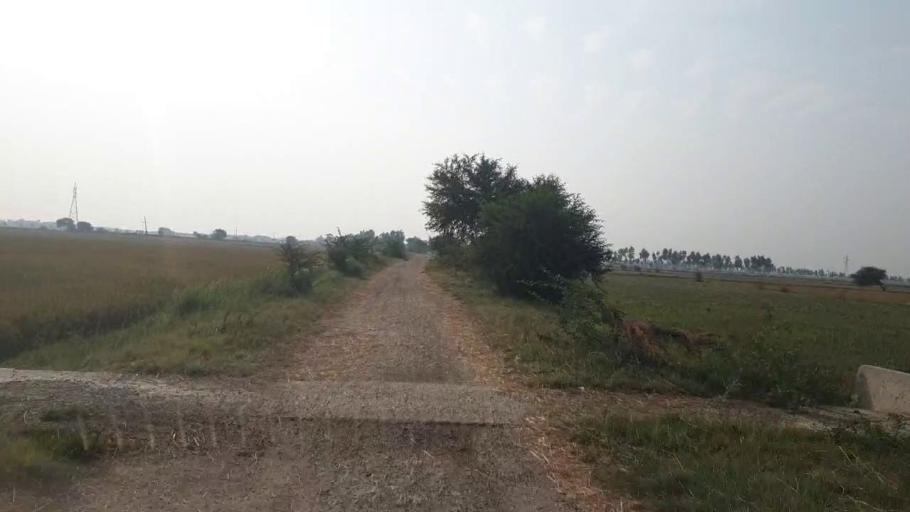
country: PK
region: Sindh
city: Tando Muhammad Khan
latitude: 25.1014
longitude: 68.5018
